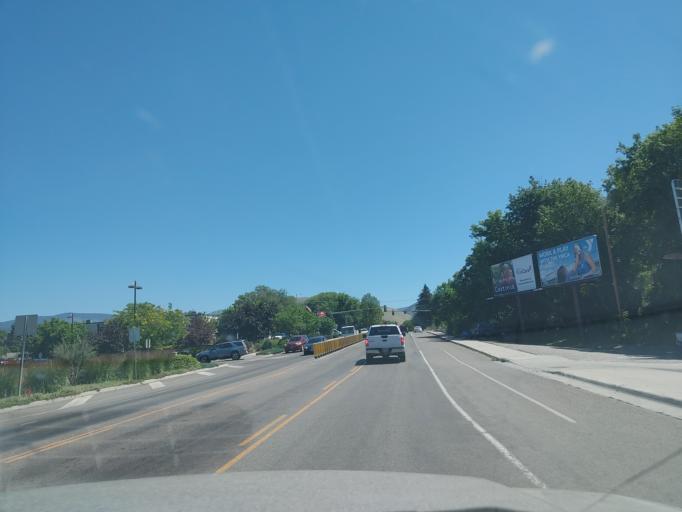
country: US
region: Montana
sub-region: Missoula County
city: Missoula
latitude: 46.8670
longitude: -114.0205
